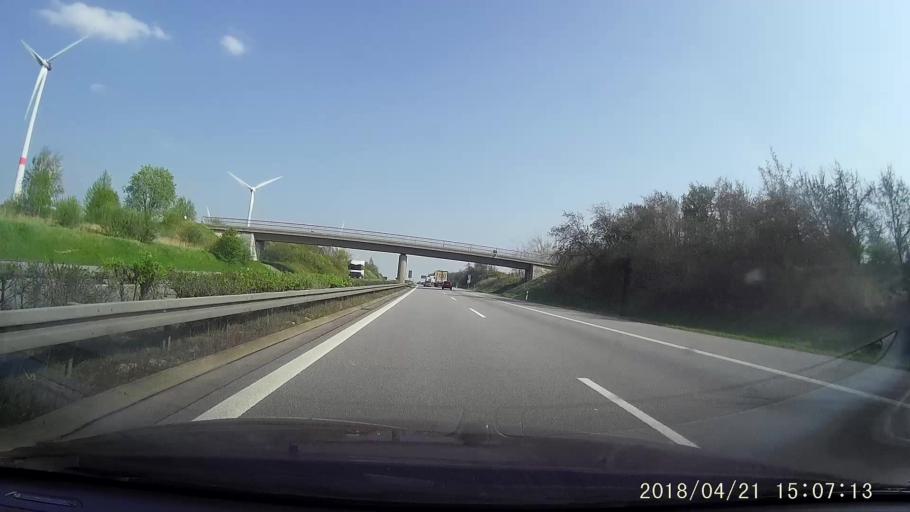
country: DE
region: Saxony
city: Goerlitz
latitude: 51.2019
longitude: 14.9545
